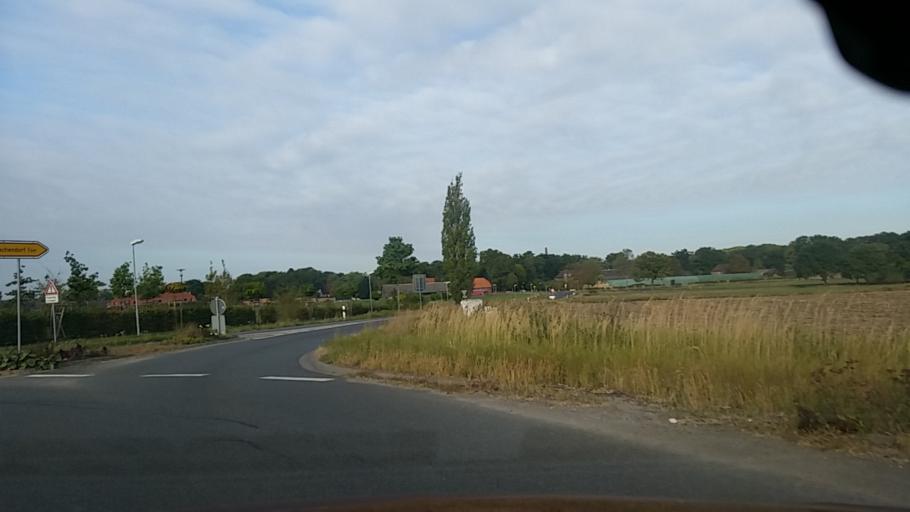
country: DE
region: Lower Saxony
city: Lachendorf
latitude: 52.6203
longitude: 10.2581
